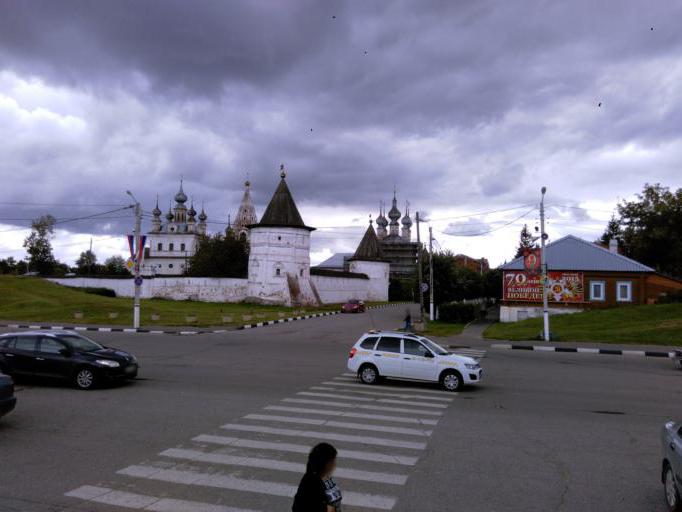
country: RU
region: Vladimir
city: Yur'yev-Pol'skiy
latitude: 56.4993
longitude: 39.6812
